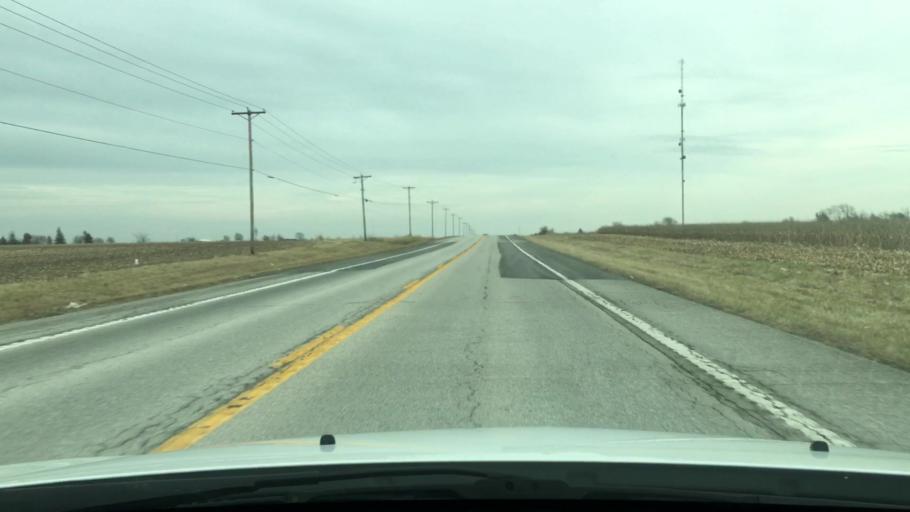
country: US
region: Missouri
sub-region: Pike County
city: Bowling Green
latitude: 39.3448
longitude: -91.3129
